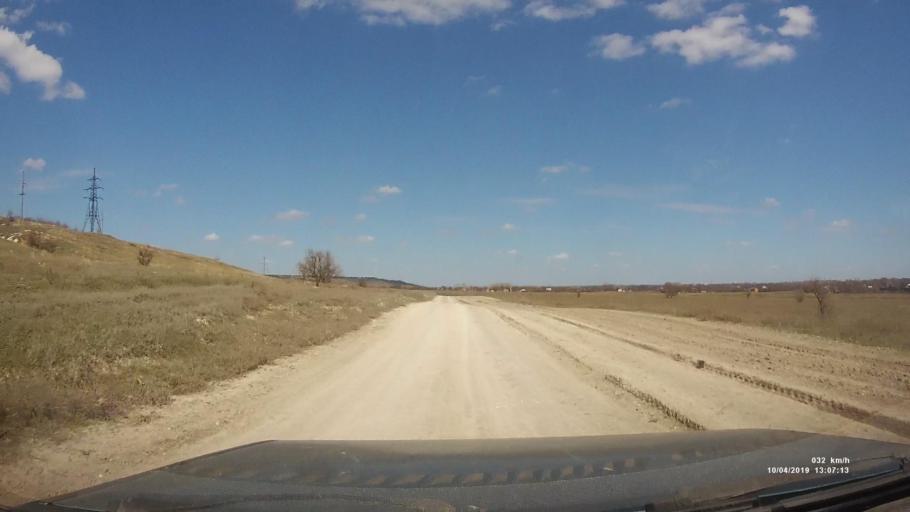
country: RU
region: Rostov
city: Masalovka
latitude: 48.3951
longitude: 40.2398
